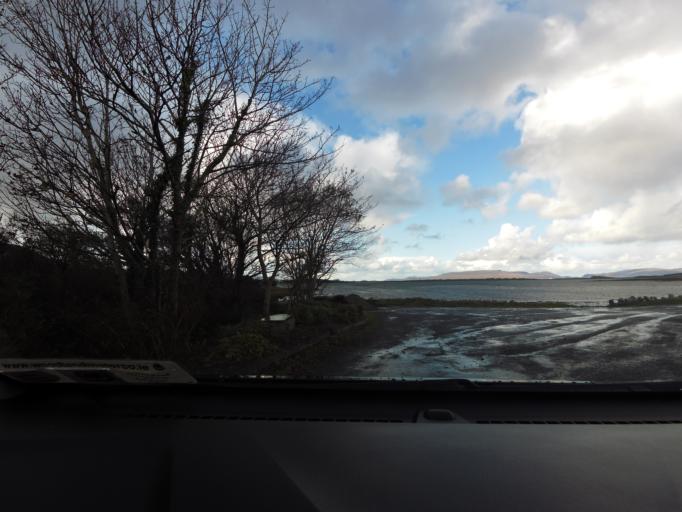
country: IE
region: Connaught
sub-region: Maigh Eo
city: Westport
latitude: 53.7819
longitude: -9.6399
